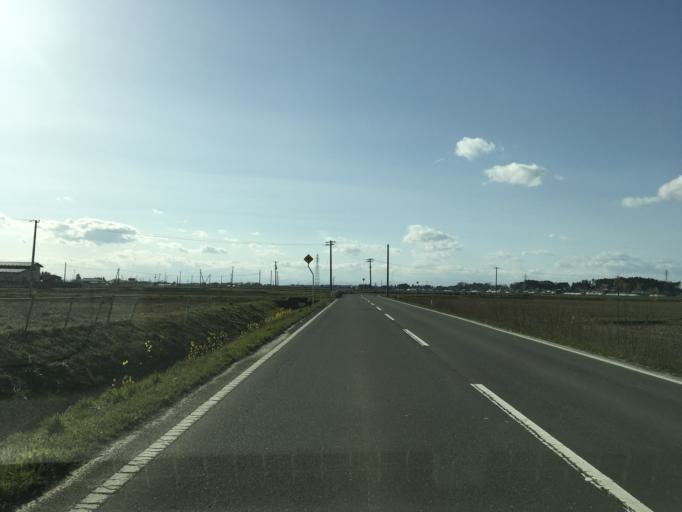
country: JP
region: Miyagi
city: Wakuya
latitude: 38.6586
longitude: 141.2313
